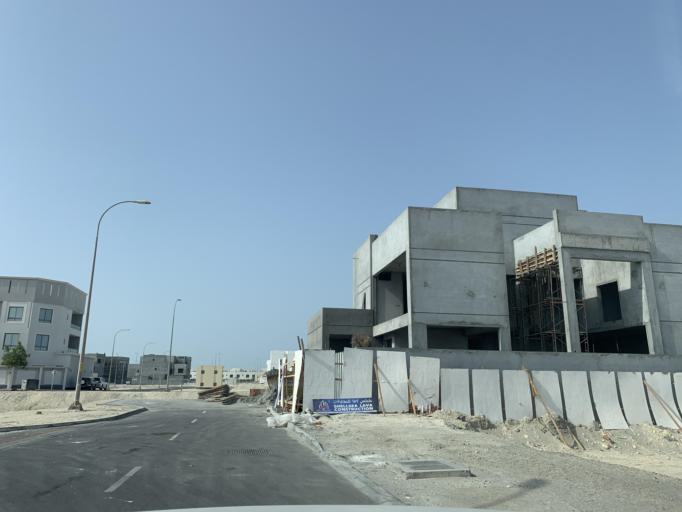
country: BH
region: Muharraq
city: Al Muharraq
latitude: 26.3096
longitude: 50.6349
